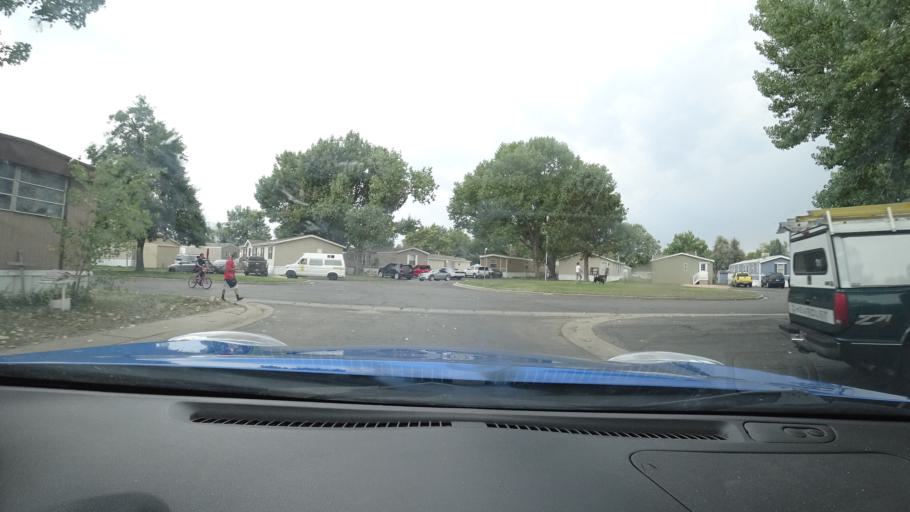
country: US
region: Colorado
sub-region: Adams County
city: Aurora
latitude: 39.7447
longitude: -104.7857
